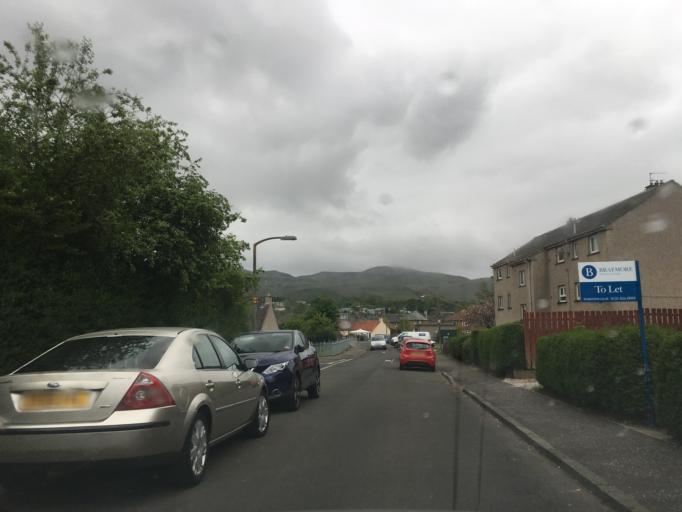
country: GB
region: Scotland
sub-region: Edinburgh
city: Colinton
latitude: 55.9127
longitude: -3.2308
